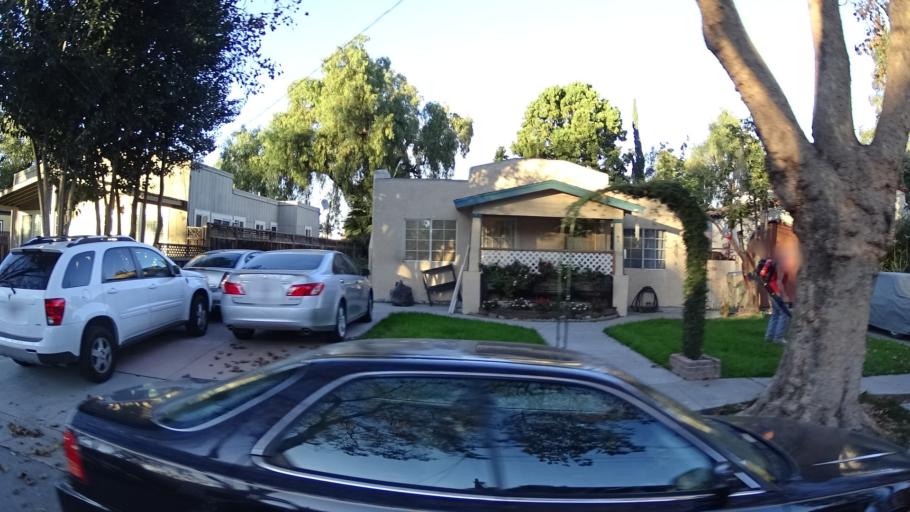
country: US
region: California
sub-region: Santa Clara County
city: Burbank
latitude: 37.3454
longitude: -121.9295
